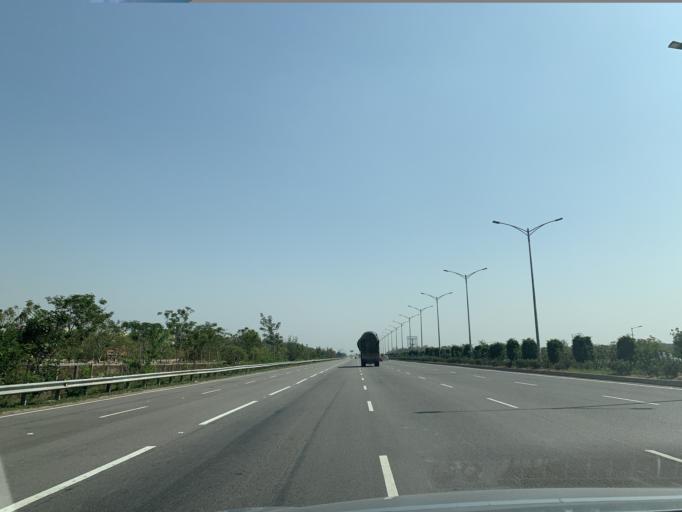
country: IN
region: Telangana
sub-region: Hyderabad
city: Hyderabad
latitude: 17.3591
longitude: 78.3550
